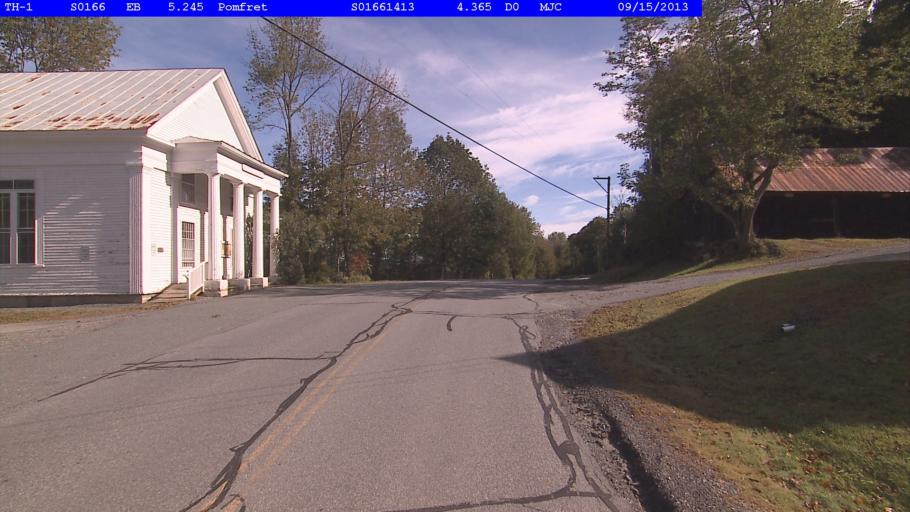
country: US
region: Vermont
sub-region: Windsor County
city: Woodstock
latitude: 43.7055
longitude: -72.5151
